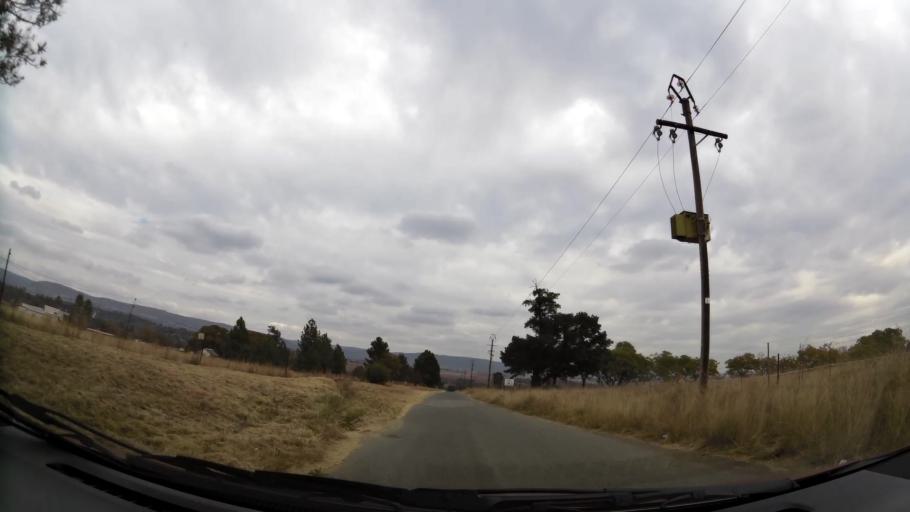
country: ZA
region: Gauteng
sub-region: West Rand District Municipality
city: Muldersdriseloop
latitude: -26.0556
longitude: 27.8857
